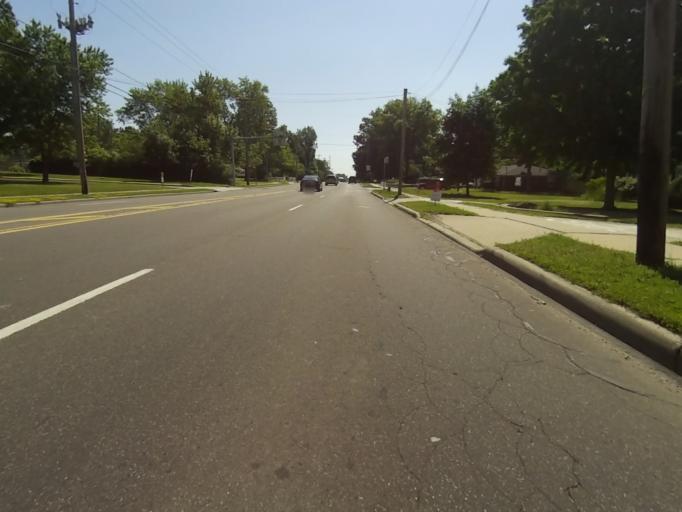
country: US
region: Ohio
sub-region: Summit County
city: Stow
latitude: 41.1667
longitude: -81.4476
